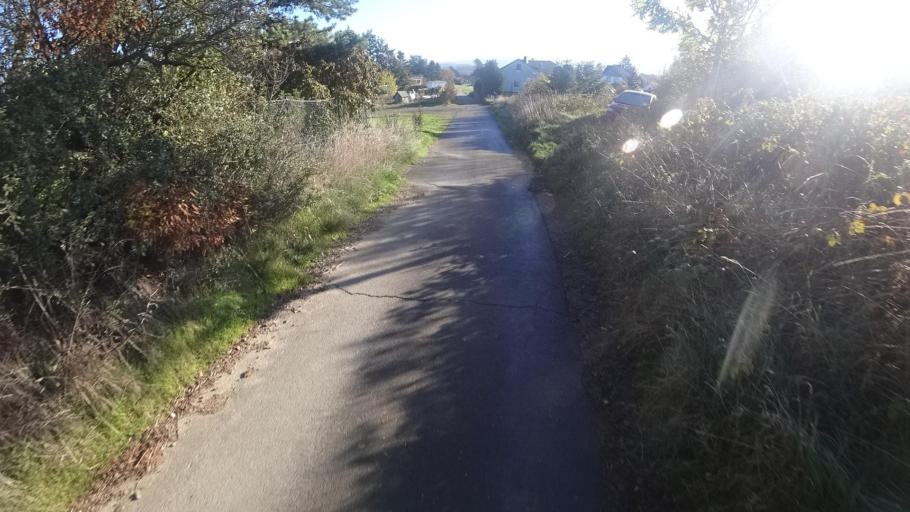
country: DE
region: Rheinland-Pfalz
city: Berg
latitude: 50.5274
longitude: 6.9429
